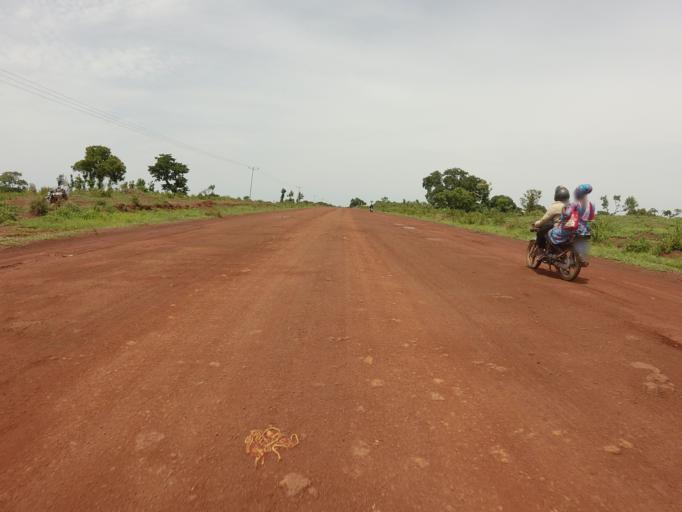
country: GH
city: Kpandae
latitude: 8.8251
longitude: 0.0619
